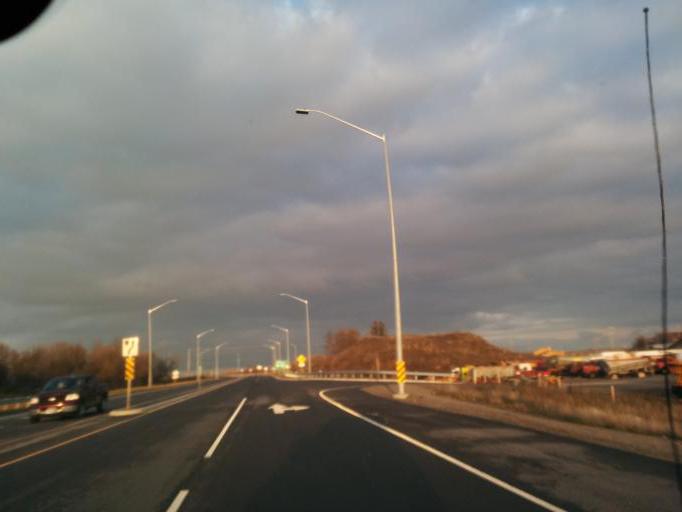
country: CA
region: Ontario
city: Brampton
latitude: 43.8966
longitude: -79.7676
